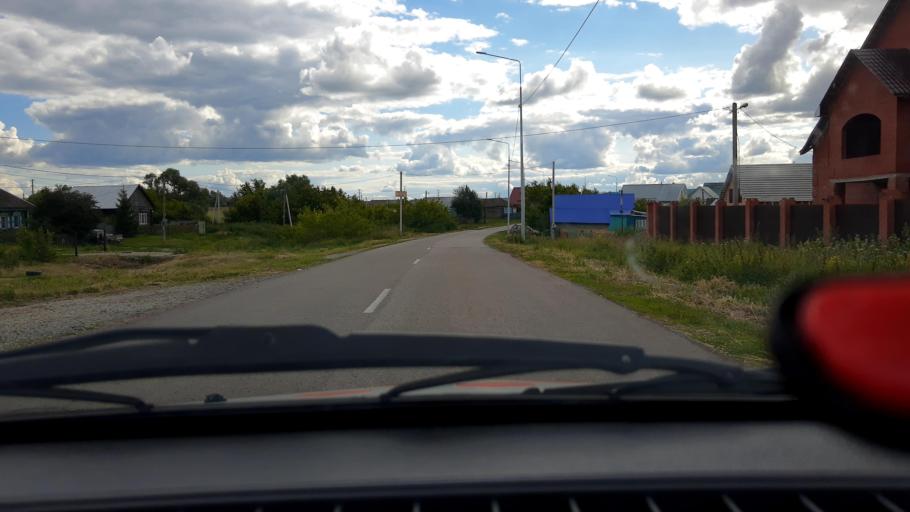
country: RU
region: Bashkortostan
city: Kabakovo
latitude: 54.5037
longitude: 55.9243
